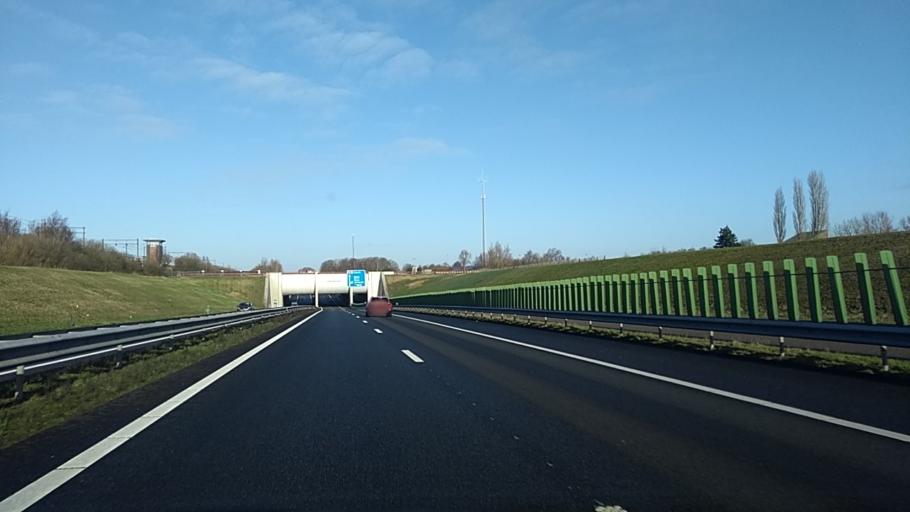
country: NL
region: Friesland
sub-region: Gemeente Boarnsterhim
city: Grou
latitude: 53.0766
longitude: 5.8302
